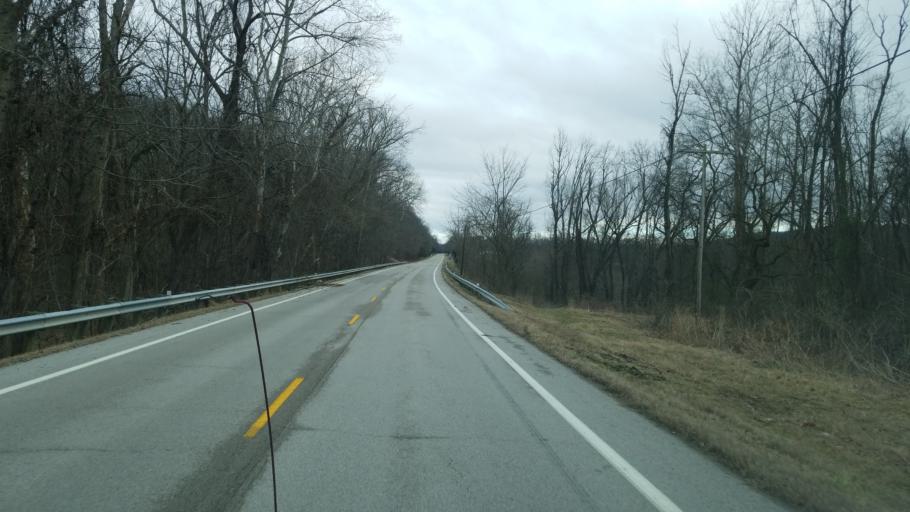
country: US
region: Kentucky
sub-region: Lewis County
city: Vanceburg
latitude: 38.6549
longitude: -83.3495
